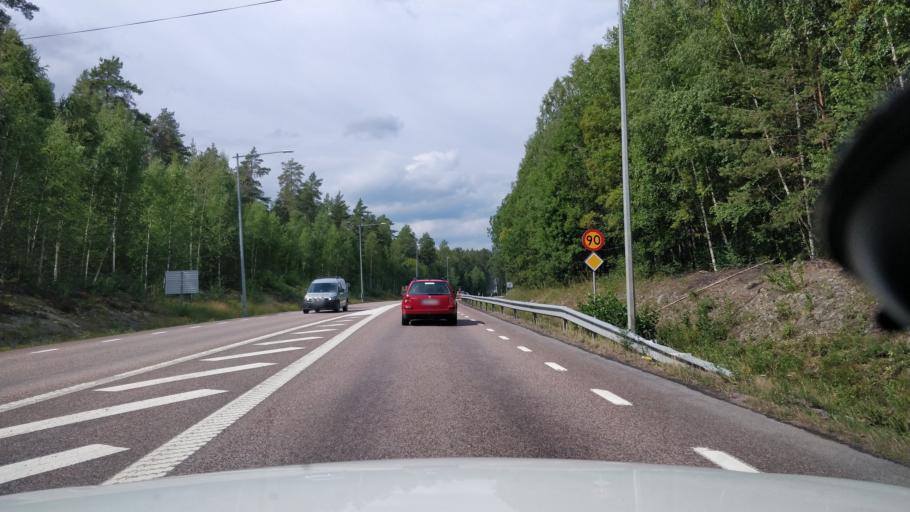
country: SE
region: Dalarna
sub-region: Faluns Kommun
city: Falun
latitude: 60.6294
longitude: 15.6004
